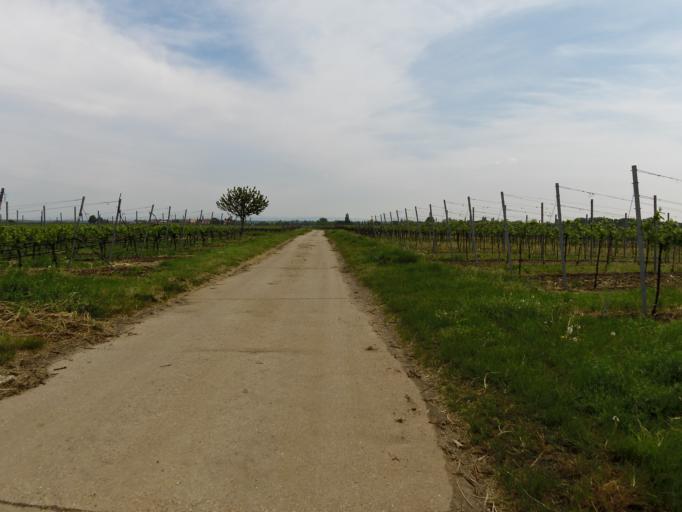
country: DE
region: Rheinland-Pfalz
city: Freinsheim
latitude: 49.4876
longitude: 8.2016
